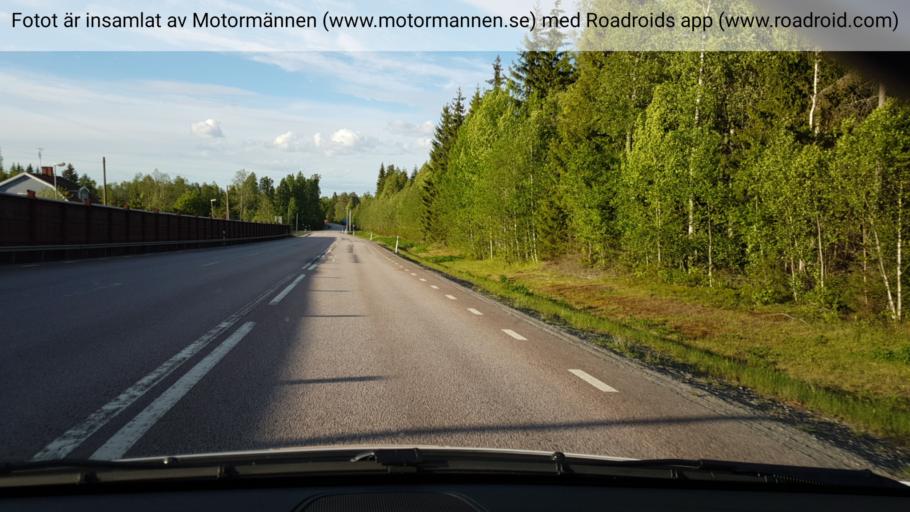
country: SE
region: Vaestmanland
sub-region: Fagersta Kommun
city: Fagersta
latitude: 59.9568
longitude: 15.7572
